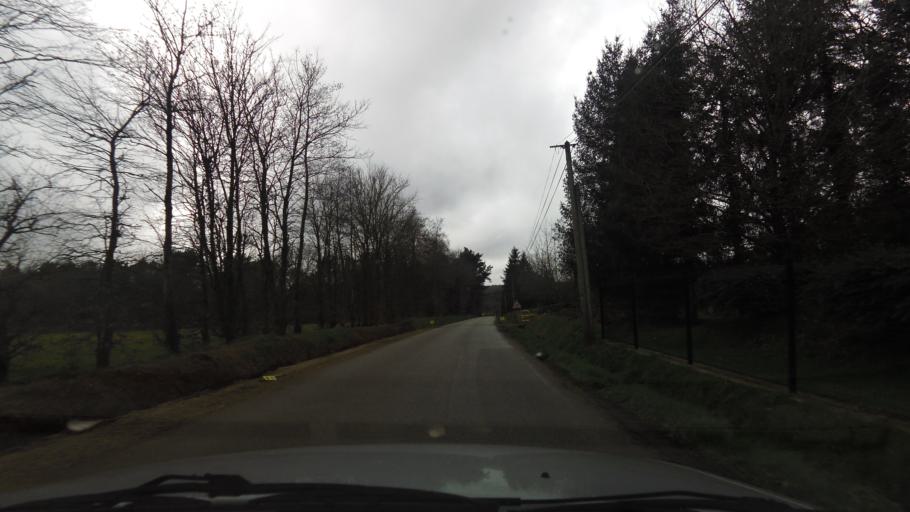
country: FR
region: Brittany
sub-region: Departement du Morbihan
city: Serent
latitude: 47.7772
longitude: -2.5339
